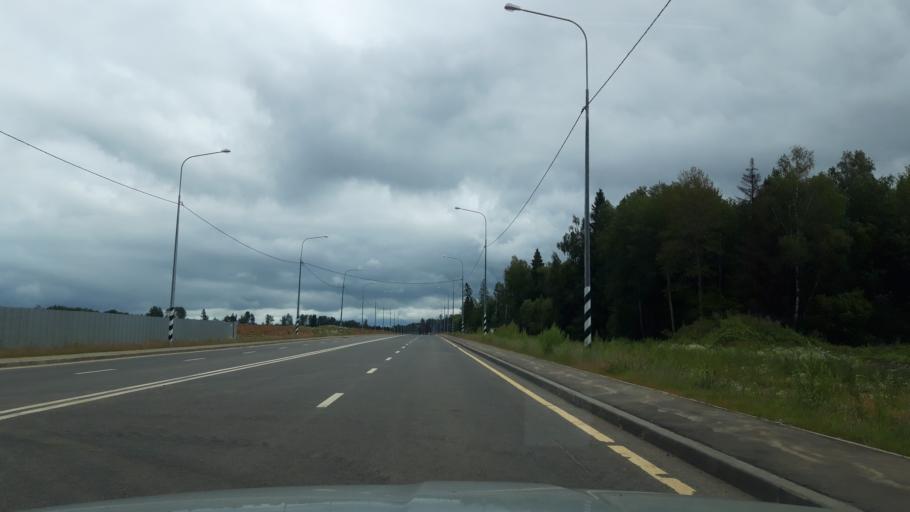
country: RU
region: Moskovskaya
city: Lozhki
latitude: 56.0802
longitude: 37.0965
